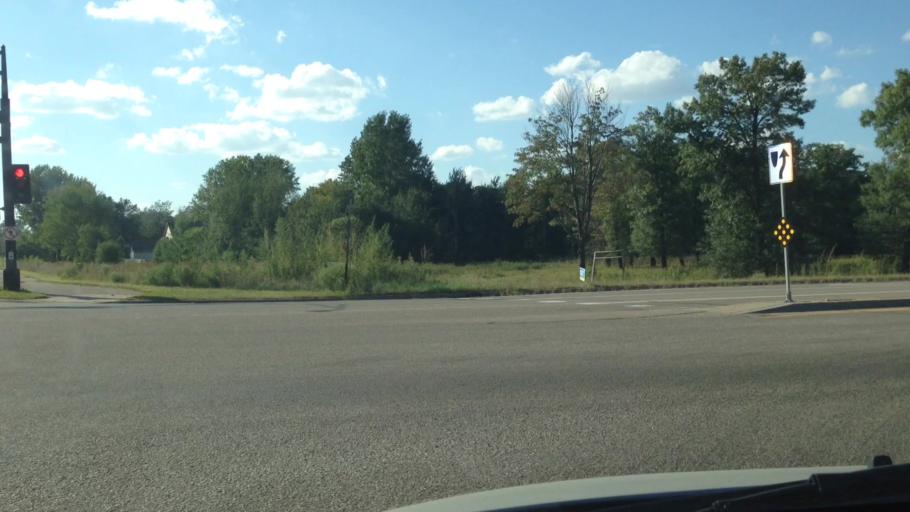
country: US
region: Minnesota
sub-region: Ramsey County
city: Mounds View
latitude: 45.1246
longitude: -93.1927
